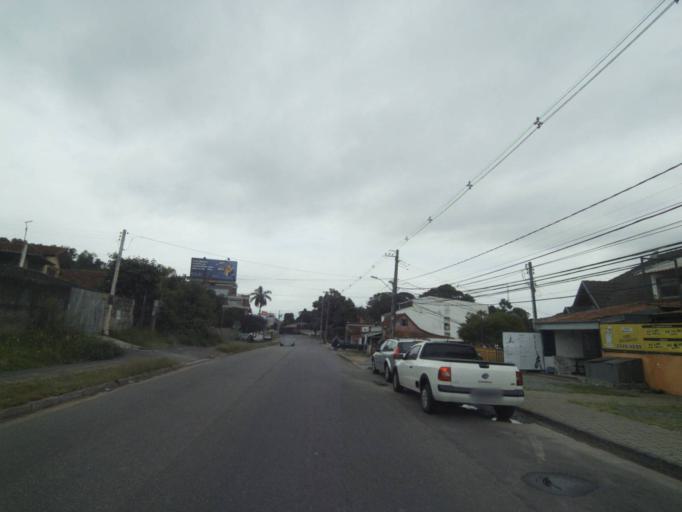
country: BR
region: Parana
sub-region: Curitiba
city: Curitiba
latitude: -25.4170
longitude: -49.2938
